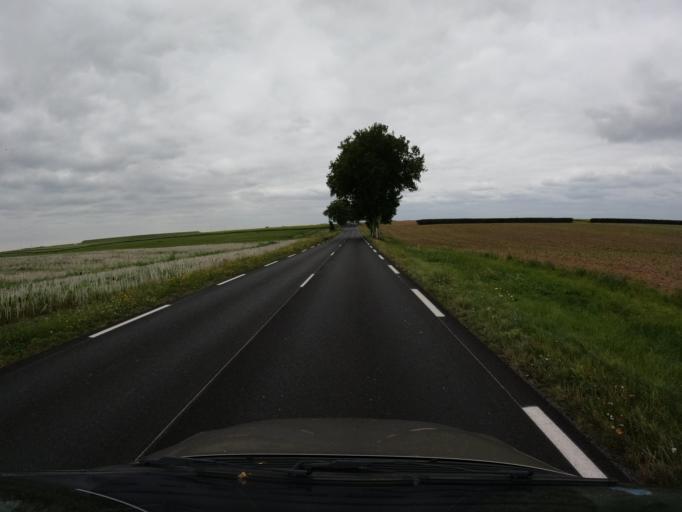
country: FR
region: Pays de la Loire
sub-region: Departement de la Vendee
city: Le Langon
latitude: 46.4956
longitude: -0.9193
